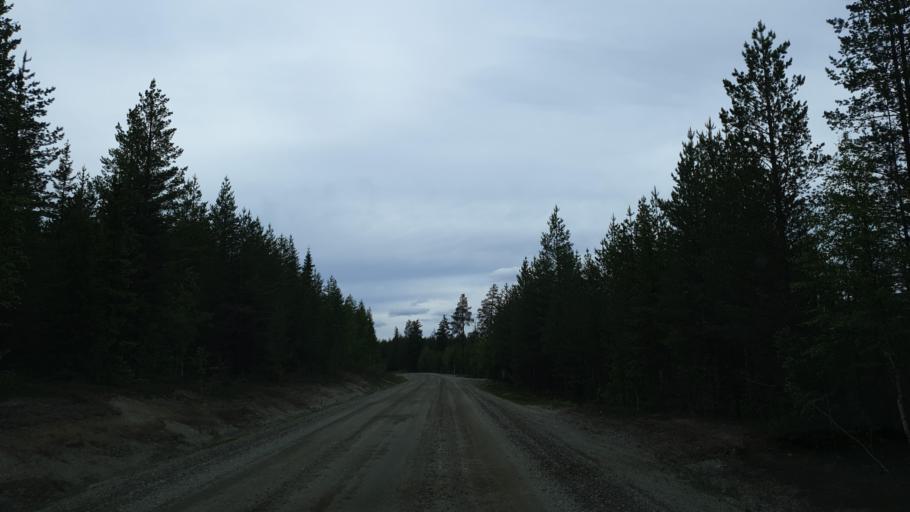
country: SE
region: Vaesterbotten
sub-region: Sorsele Kommun
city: Sorsele
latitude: 65.5547
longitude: 17.5061
